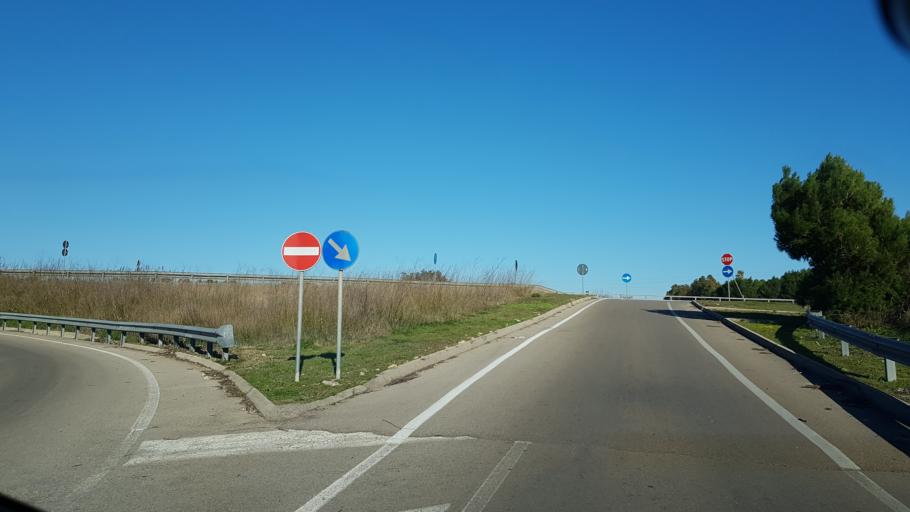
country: IT
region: Apulia
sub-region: Provincia di Lecce
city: Gallipoli
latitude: 40.0392
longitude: 18.0201
